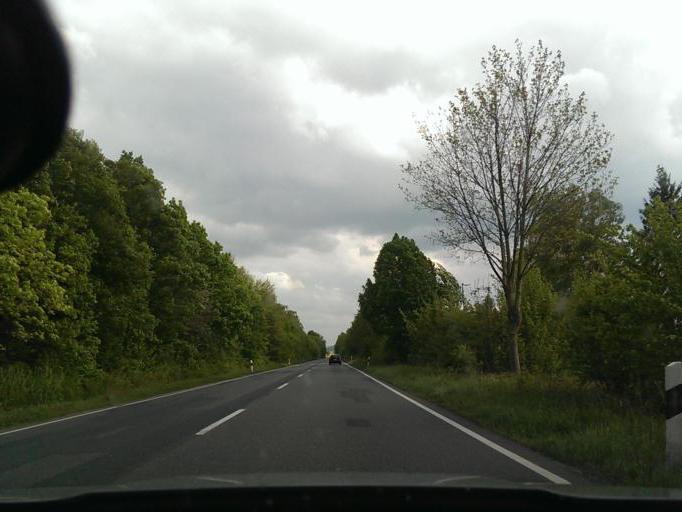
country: DE
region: Lower Saxony
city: Banteln
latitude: 52.0716
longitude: 9.7459
